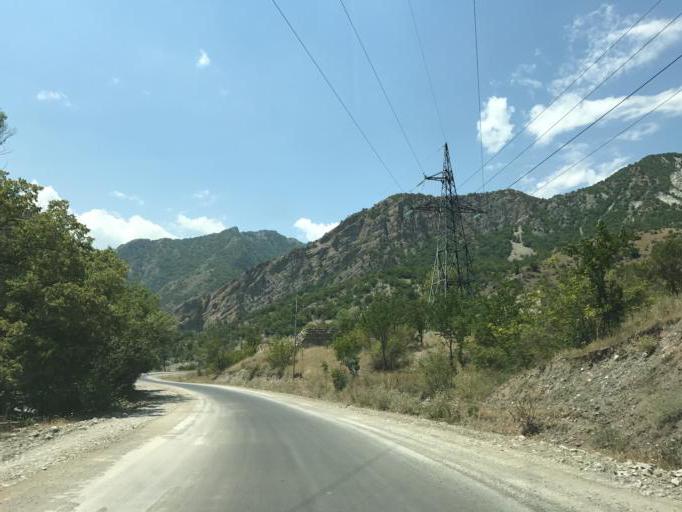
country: AZ
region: Kalbacar Rayonu
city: Kerbakhiar
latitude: 40.1627
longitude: 46.2261
